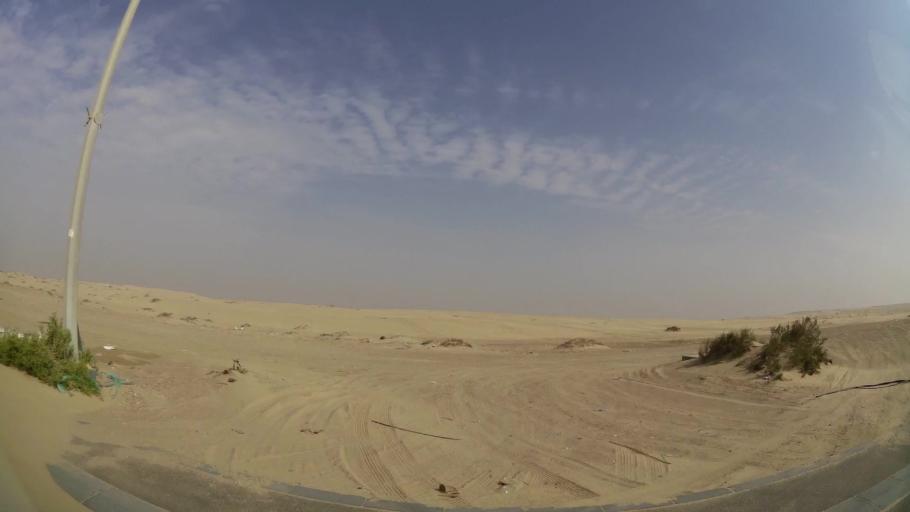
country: AE
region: Abu Dhabi
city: Abu Dhabi
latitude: 24.2802
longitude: 54.6949
